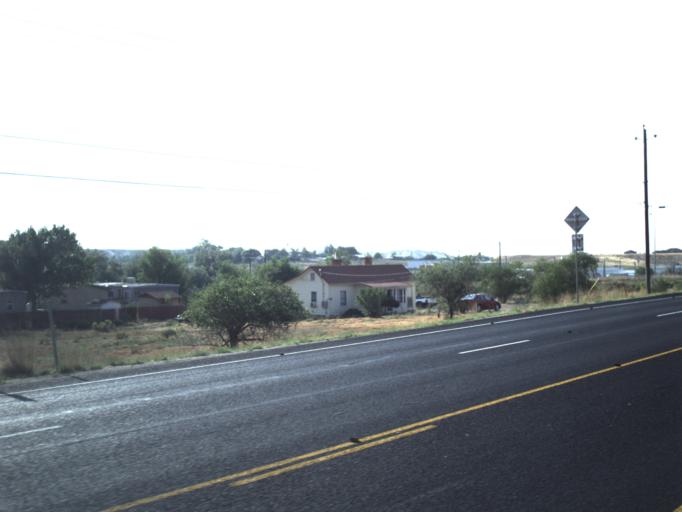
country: US
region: Utah
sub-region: Carbon County
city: Price
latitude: 39.5903
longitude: -110.7896
